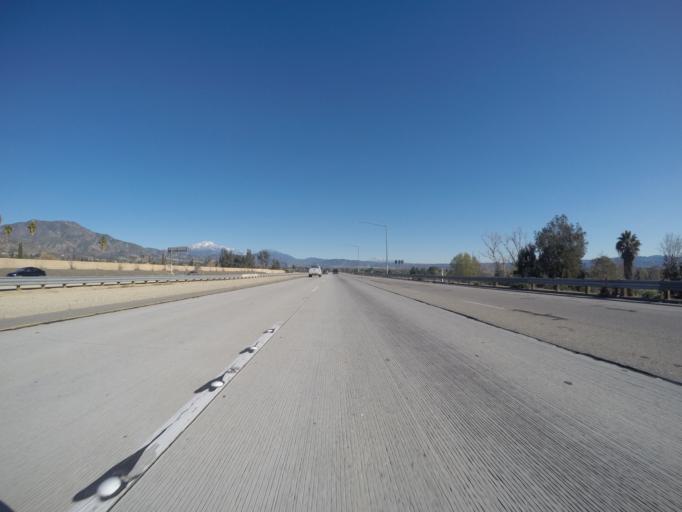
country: US
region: California
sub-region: San Bernardino County
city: Highland
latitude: 34.1340
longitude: -117.2318
